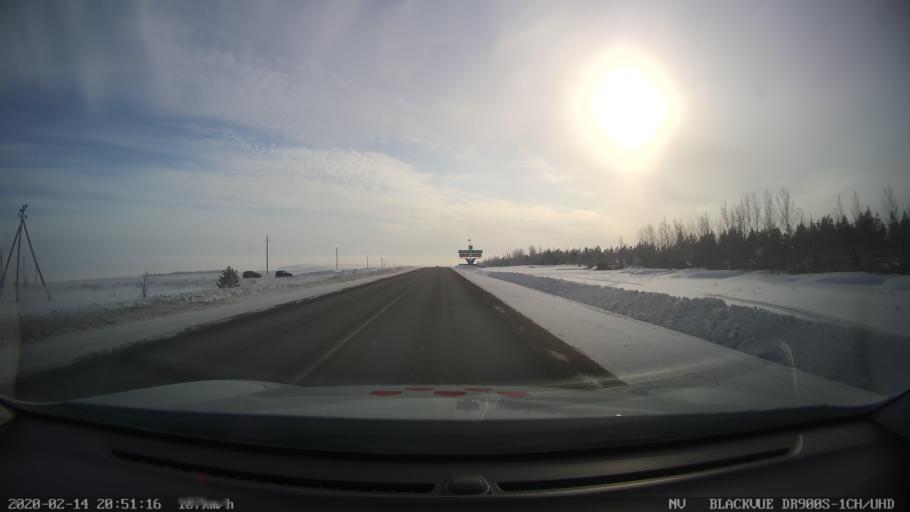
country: RU
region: Tatarstan
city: Kuybyshevskiy Zaton
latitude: 55.2152
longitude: 49.2366
